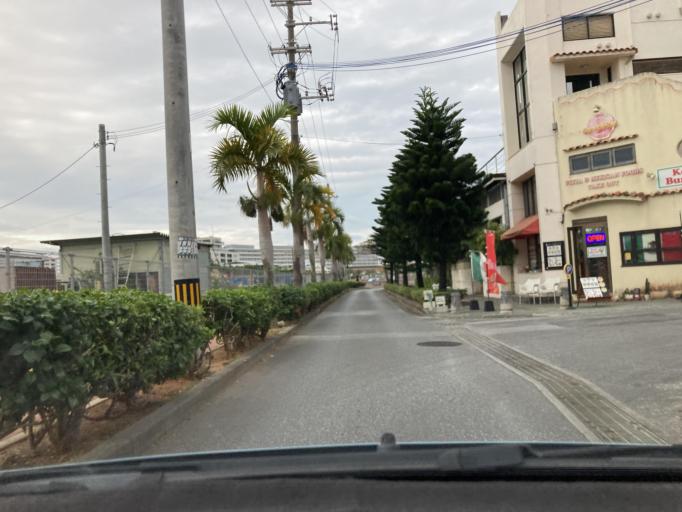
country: JP
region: Okinawa
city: Chatan
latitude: 26.3225
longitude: 127.7519
